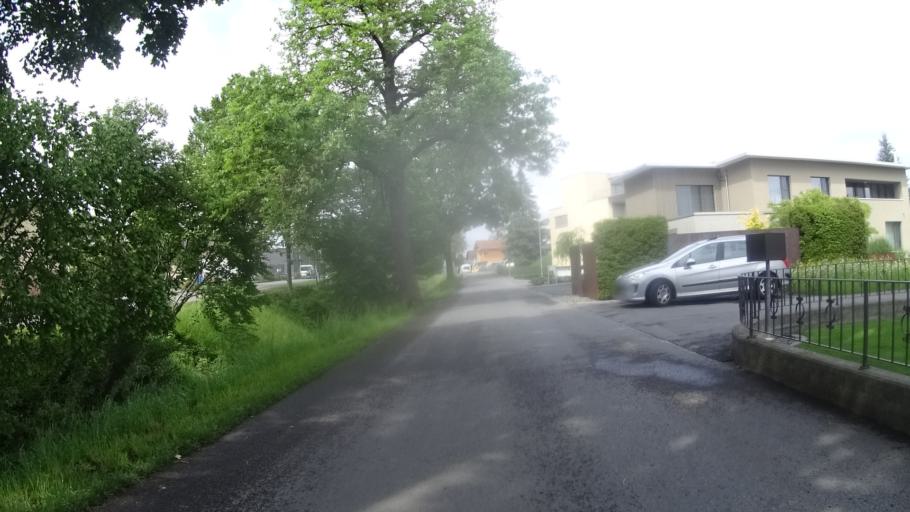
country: AT
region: Vorarlberg
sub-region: Politischer Bezirk Feldkirch
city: Mader
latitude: 47.3669
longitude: 9.6128
